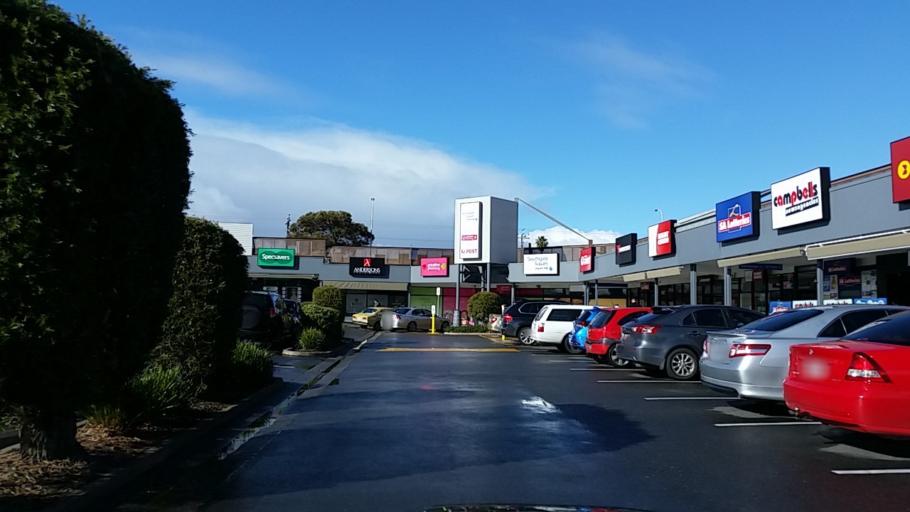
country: AU
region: South Australia
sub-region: Onkaparinga
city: Reynella
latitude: -35.1071
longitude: 138.5212
